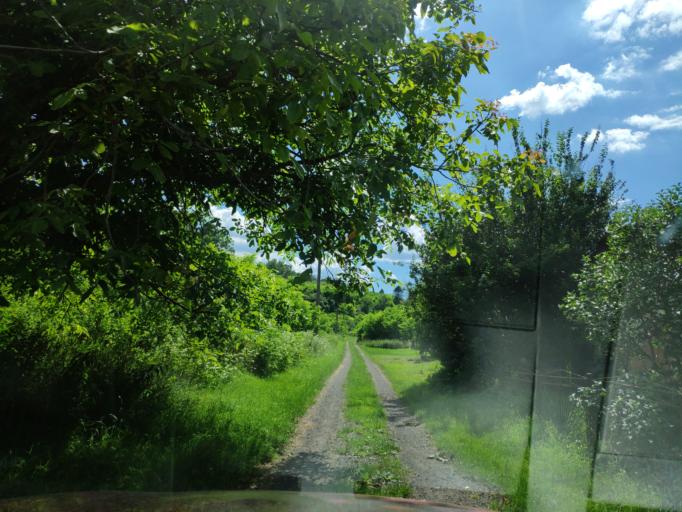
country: HU
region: Borsod-Abauj-Zemplen
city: Arlo
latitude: 48.2779
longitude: 20.1884
